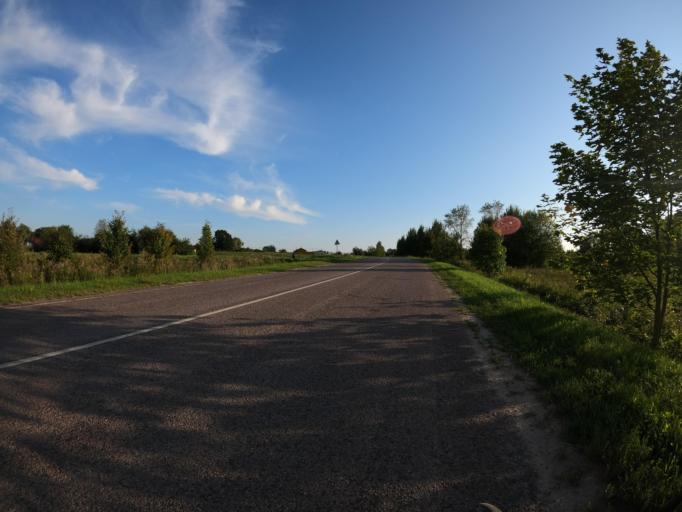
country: RU
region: Moskovskaya
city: Meshcherino
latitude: 55.1183
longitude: 38.3219
